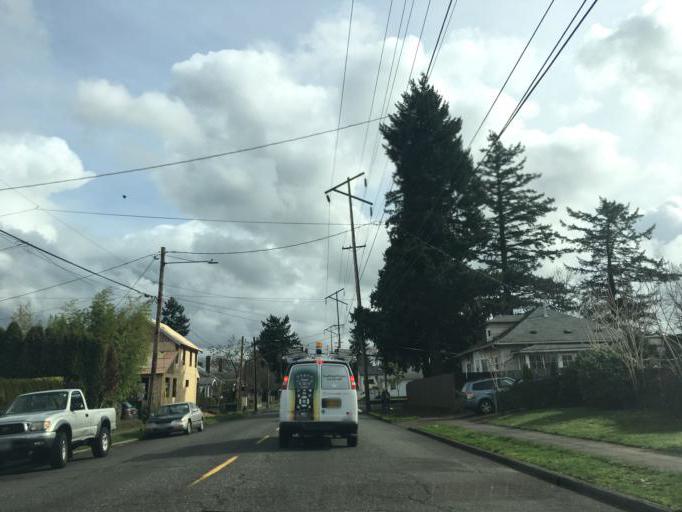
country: US
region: Oregon
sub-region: Multnomah County
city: Lents
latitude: 45.4903
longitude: -122.5901
